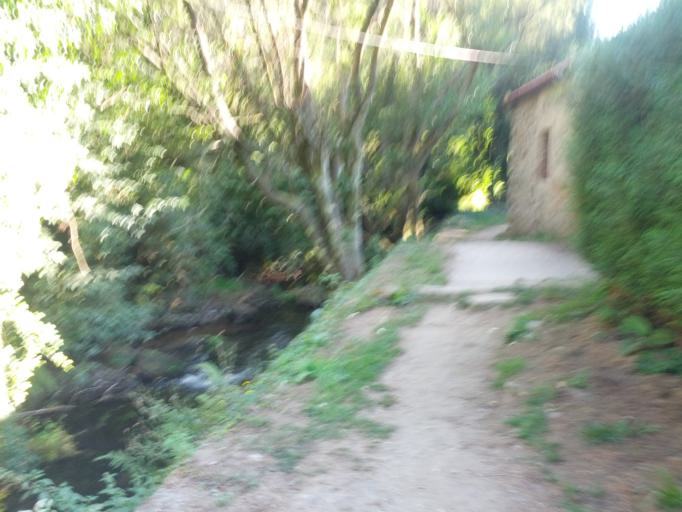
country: ES
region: Galicia
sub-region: Provincia da Coruna
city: Santiago de Compostela
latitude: 42.8800
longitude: -8.5595
